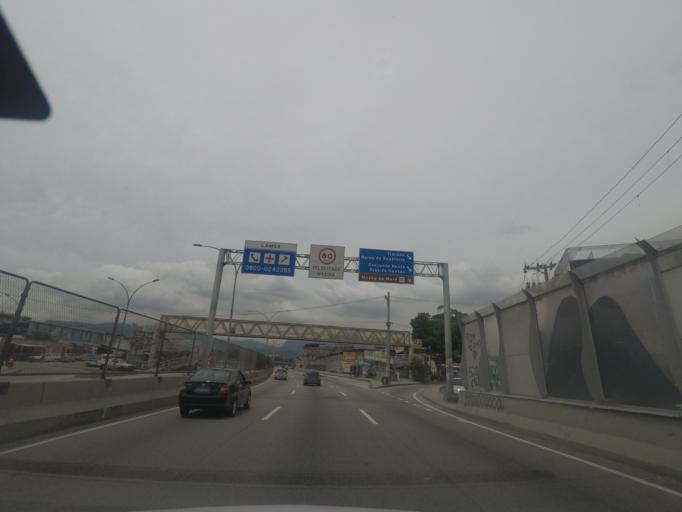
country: BR
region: Rio de Janeiro
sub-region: Rio De Janeiro
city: Rio de Janeiro
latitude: -22.8637
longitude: -43.2391
